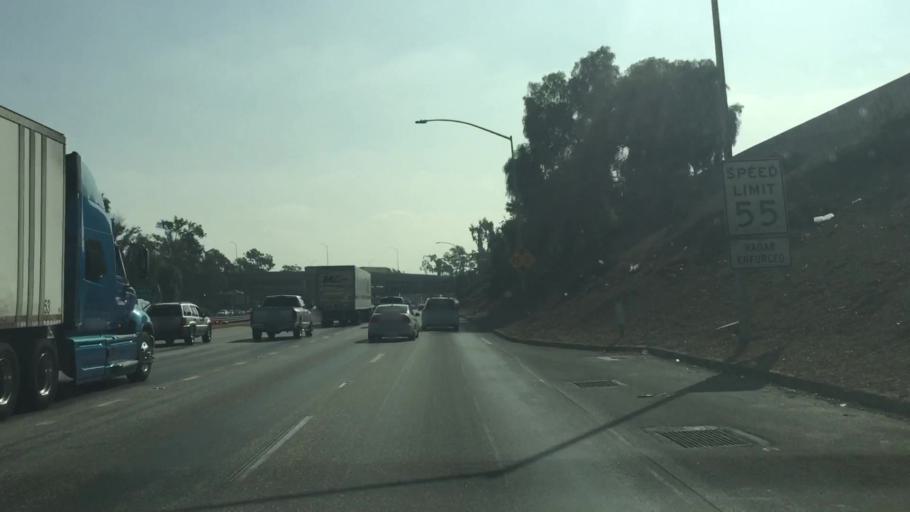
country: US
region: California
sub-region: Los Angeles County
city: East Los Angeles
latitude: 34.0182
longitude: -118.1774
